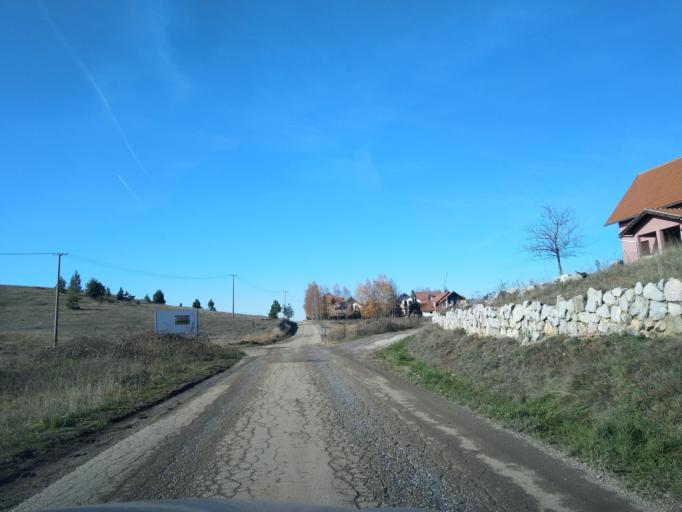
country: RS
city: Zlatibor
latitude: 43.7374
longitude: 19.6779
